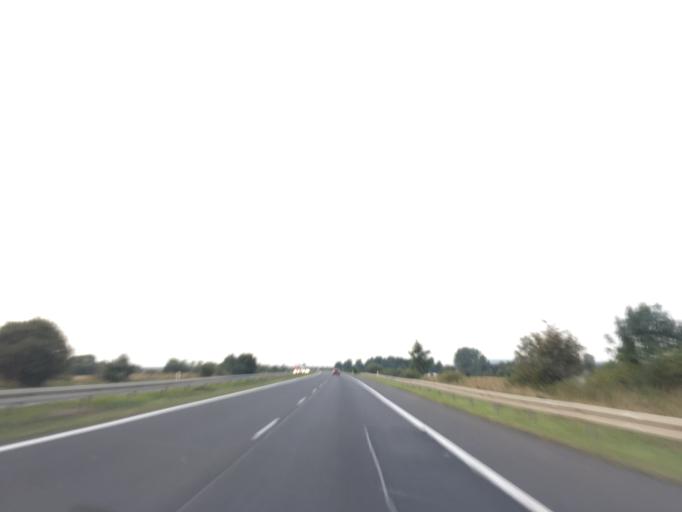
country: PL
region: Lodz Voivodeship
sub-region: Powiat piotrkowski
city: Wola Krzysztoporska
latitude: 51.2870
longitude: 19.5393
